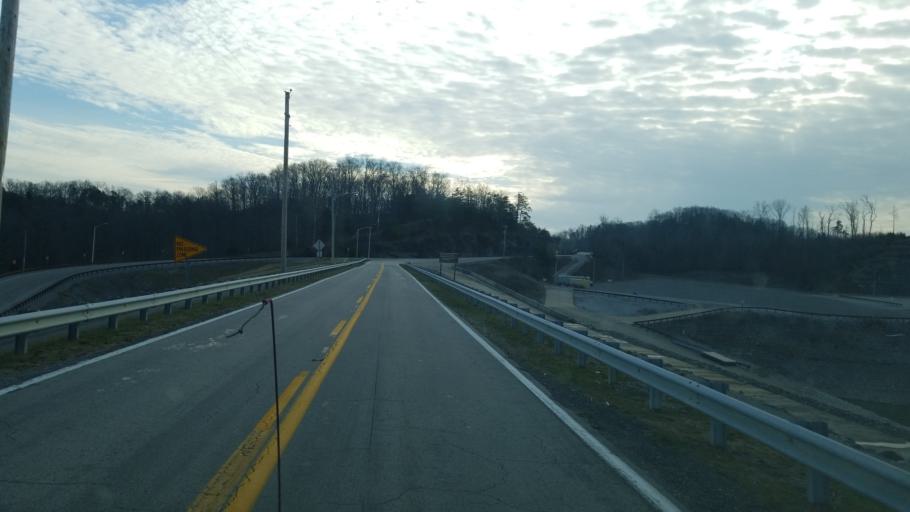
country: US
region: Kentucky
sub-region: Russell County
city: Jamestown
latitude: 36.8724
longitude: -85.1337
